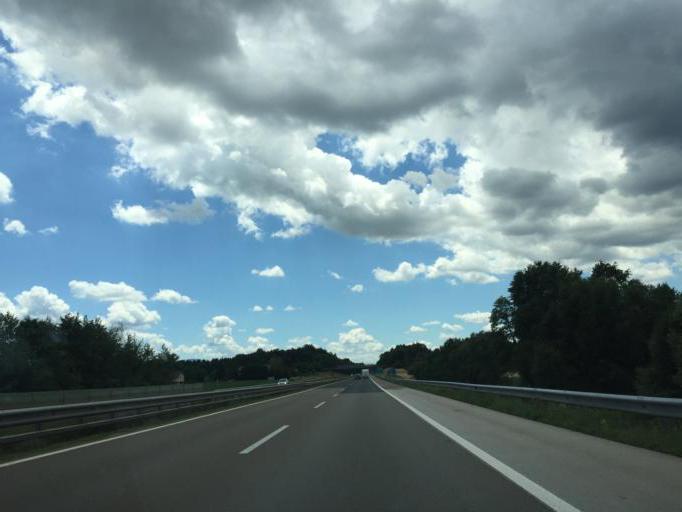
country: SI
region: Race-Fram
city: Morje
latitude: 46.4382
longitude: 15.6417
